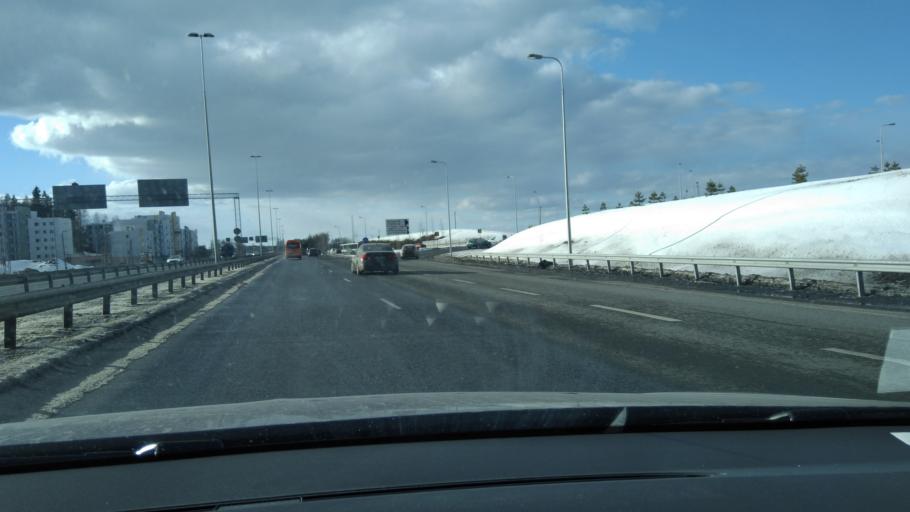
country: FI
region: Pirkanmaa
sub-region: Tampere
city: Tampere
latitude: 61.5033
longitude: 23.7246
